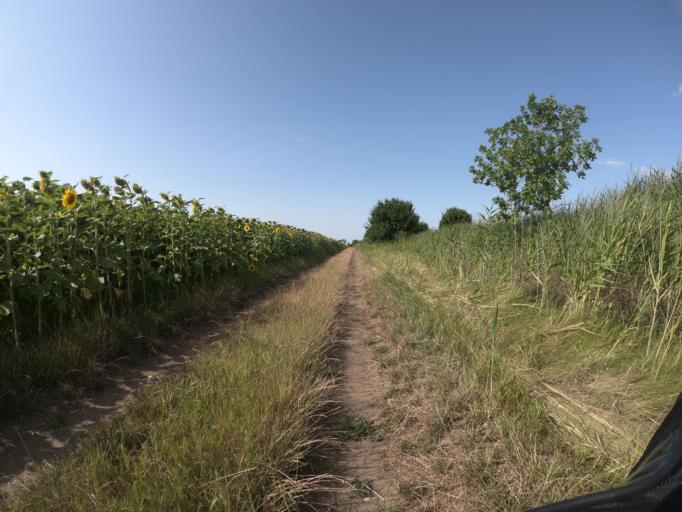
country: HU
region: Hajdu-Bihar
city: Egyek
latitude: 47.5854
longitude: 20.9614
